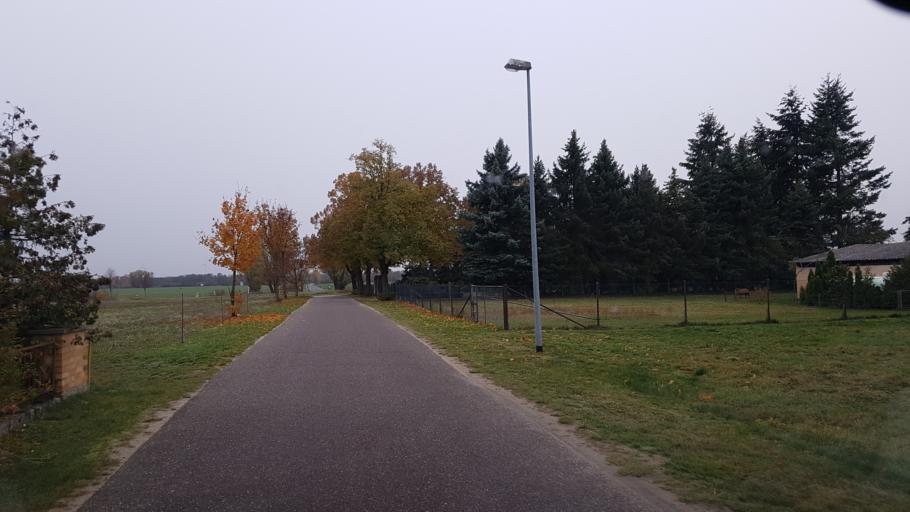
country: DE
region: Brandenburg
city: Finsterwalde
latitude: 51.6850
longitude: 13.7222
